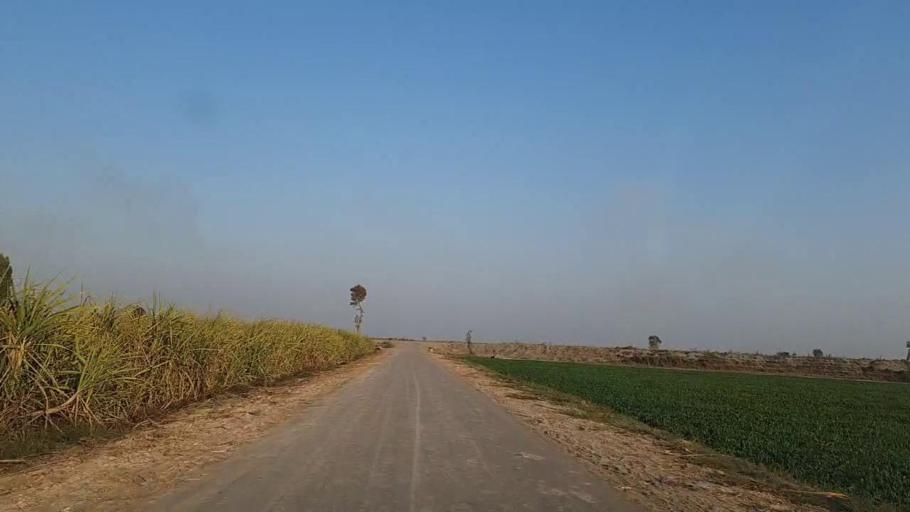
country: PK
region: Sindh
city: Daur
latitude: 26.5063
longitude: 68.2861
